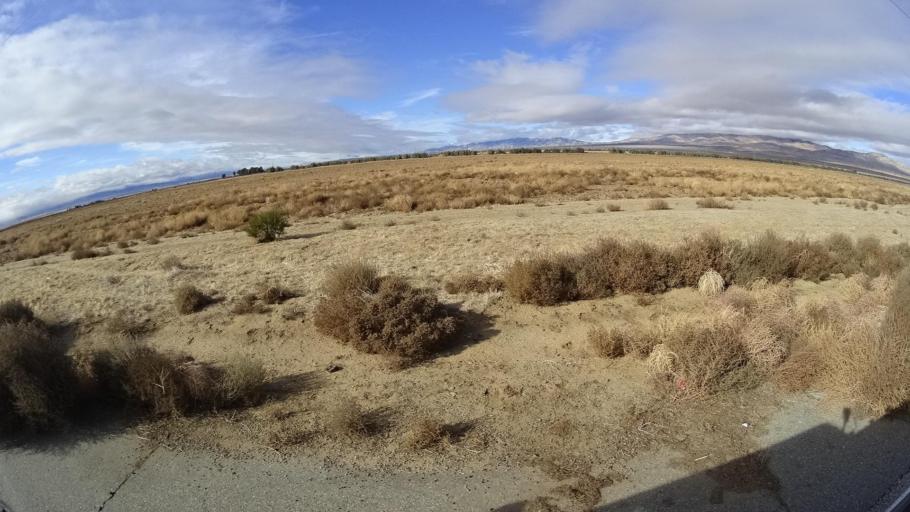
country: US
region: California
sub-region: Kern County
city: Rosamond
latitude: 34.9116
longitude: -118.2914
